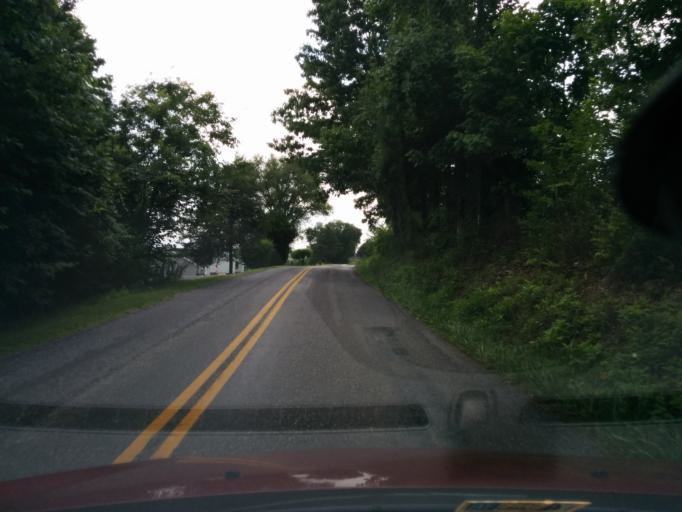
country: US
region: Virginia
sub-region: Rockbridge County
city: East Lexington
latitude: 37.8169
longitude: -79.4033
